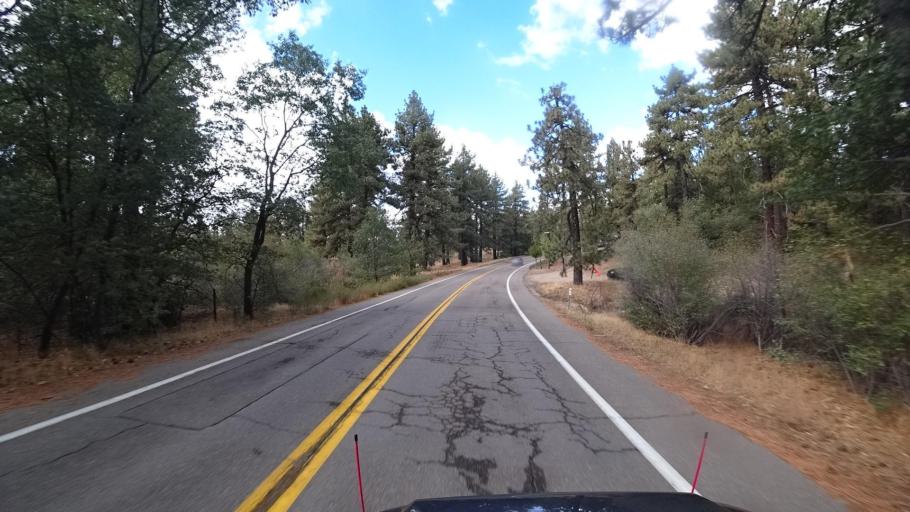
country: US
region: California
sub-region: San Diego County
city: Pine Valley
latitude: 32.8640
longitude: -116.4205
